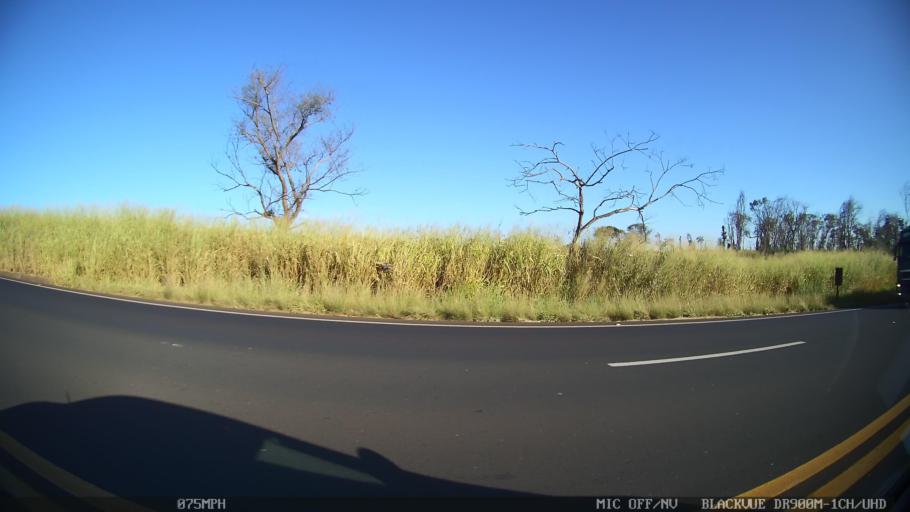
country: BR
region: Sao Paulo
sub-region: Guapiacu
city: Guapiacu
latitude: -20.7418
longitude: -49.1000
